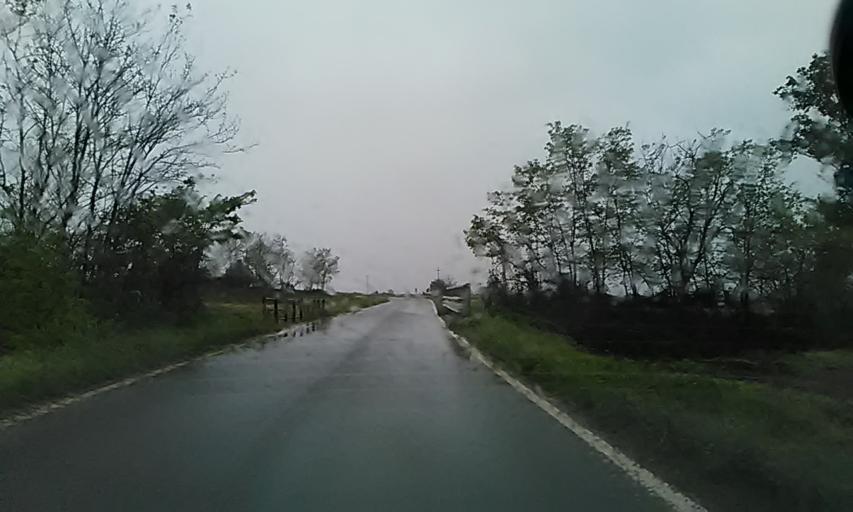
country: IT
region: Piedmont
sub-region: Provincia di Vercelli
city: Arborio
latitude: 45.4964
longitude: 8.3717
